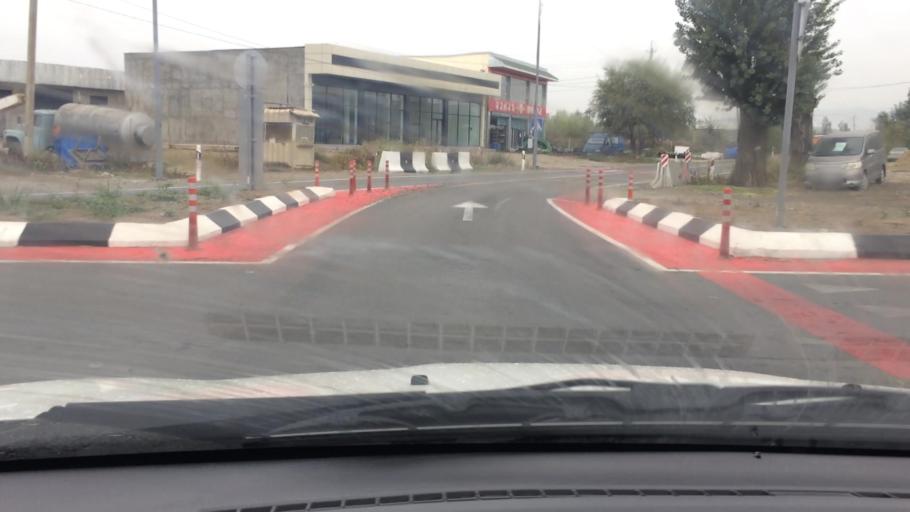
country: GE
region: Kvemo Kartli
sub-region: Marneuli
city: Marneuli
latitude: 41.4601
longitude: 44.8100
